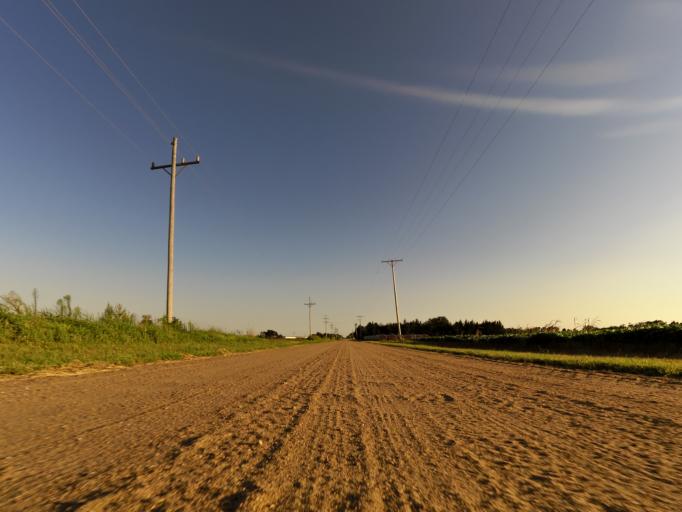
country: US
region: Kansas
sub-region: Reno County
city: South Hutchinson
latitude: 38.0028
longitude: -98.0319
